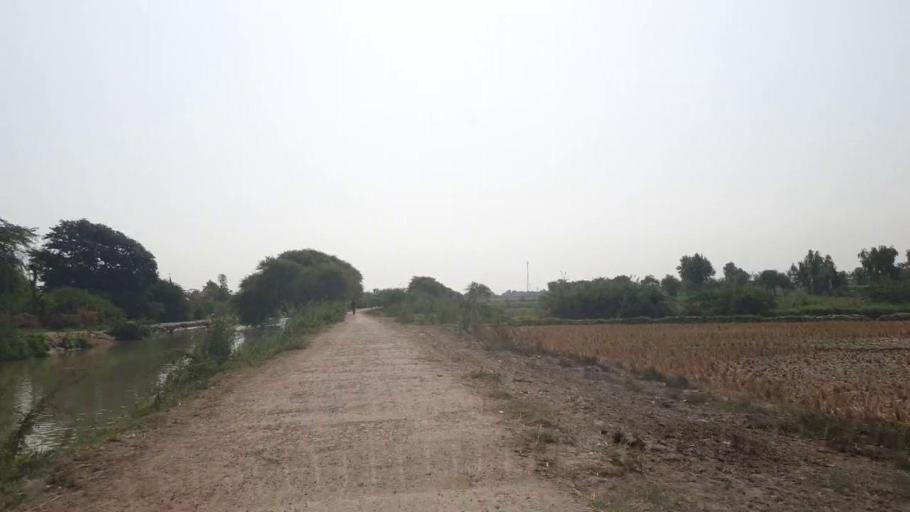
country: PK
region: Sindh
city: Badin
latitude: 24.6464
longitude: 68.8468
